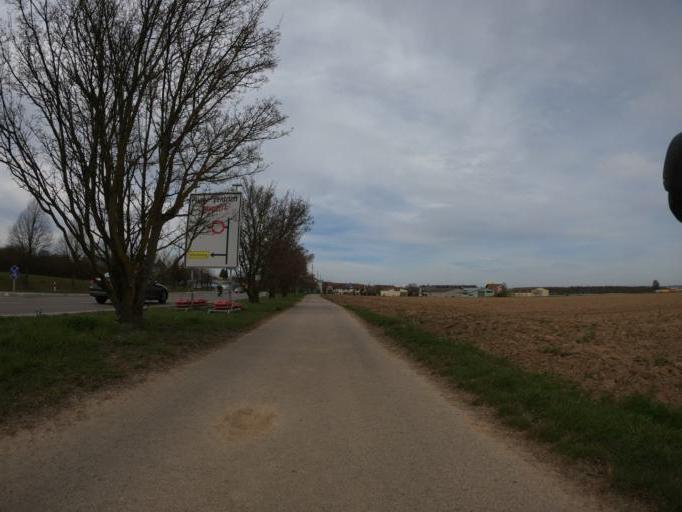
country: DE
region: Baden-Wuerttemberg
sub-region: Regierungsbezirk Stuttgart
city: Filderstadt
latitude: 48.6963
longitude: 9.2217
